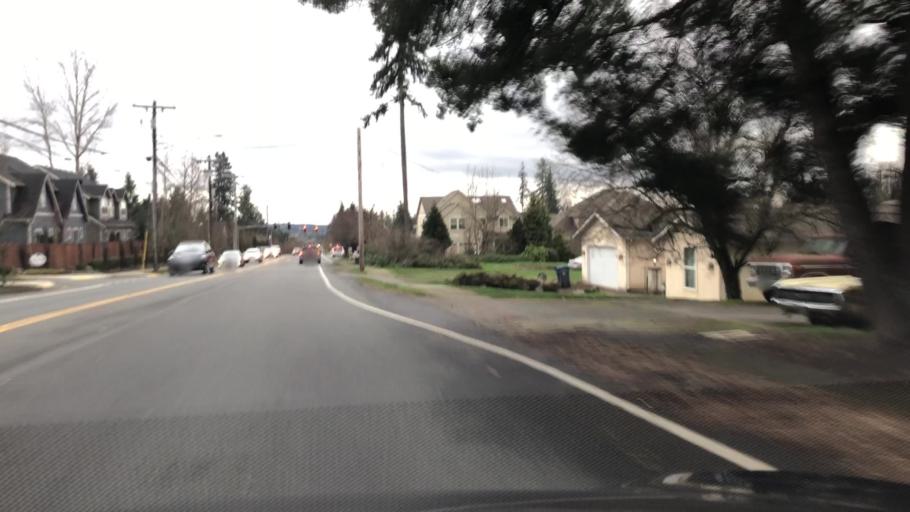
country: US
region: Washington
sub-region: Snohomish County
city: North Creek
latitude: 47.8072
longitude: -122.1808
